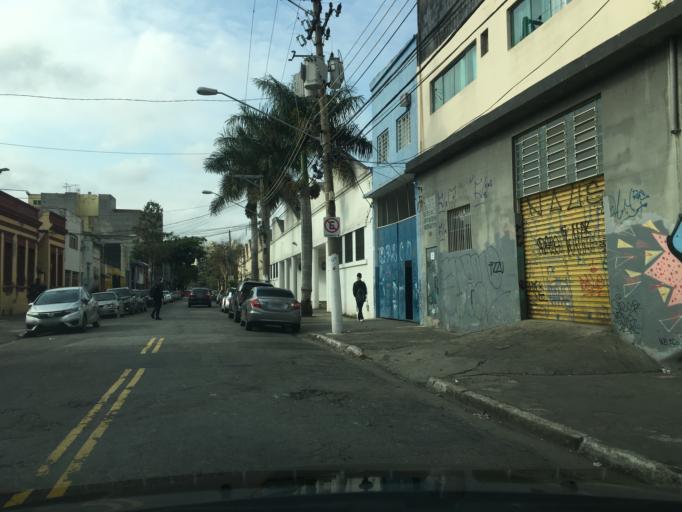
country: BR
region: Sao Paulo
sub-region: Sao Paulo
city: Sao Paulo
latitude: -23.5492
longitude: -46.6103
